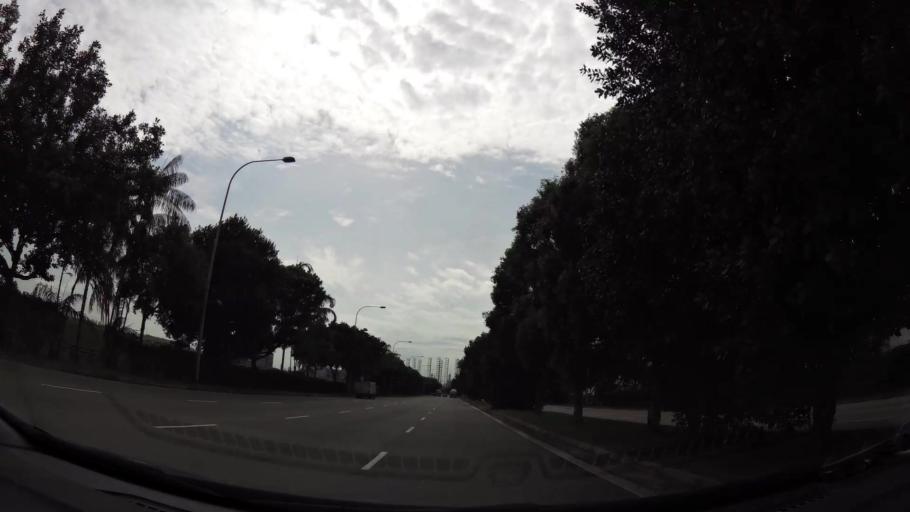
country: SG
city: Singapore
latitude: 1.3085
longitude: 103.7393
